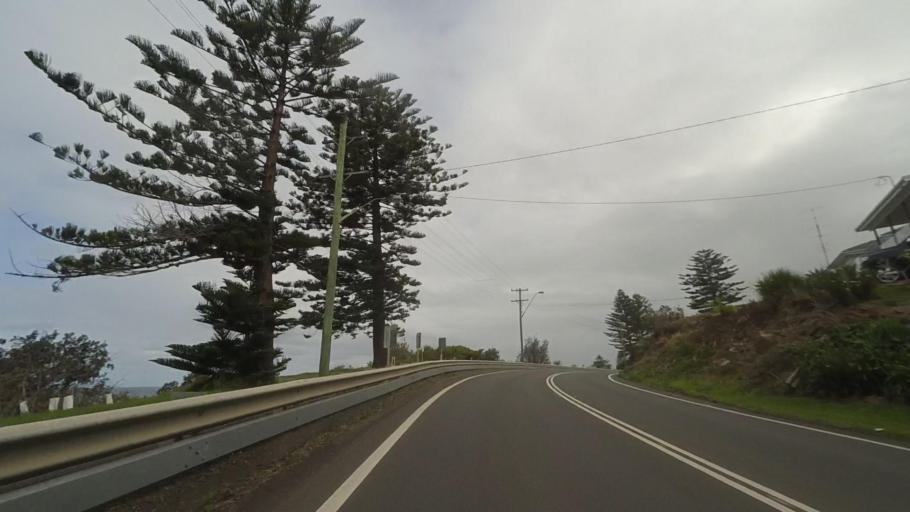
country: AU
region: New South Wales
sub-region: Wollongong
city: Bulli
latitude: -34.2982
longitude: 150.9407
